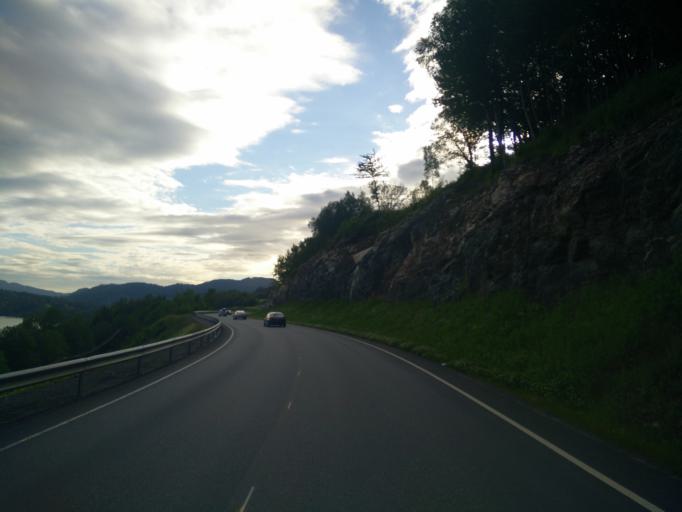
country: NO
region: More og Romsdal
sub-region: Tingvoll
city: Tingvoll
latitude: 63.0509
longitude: 8.0997
